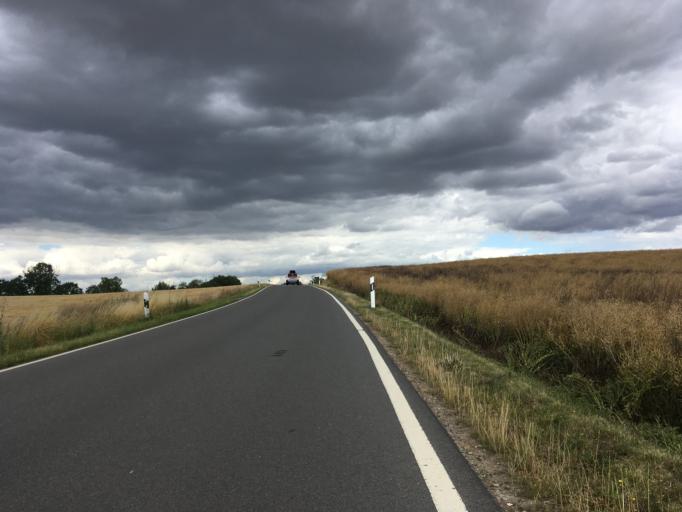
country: DE
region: Brandenburg
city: Gramzow
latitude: 53.2240
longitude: 13.9387
